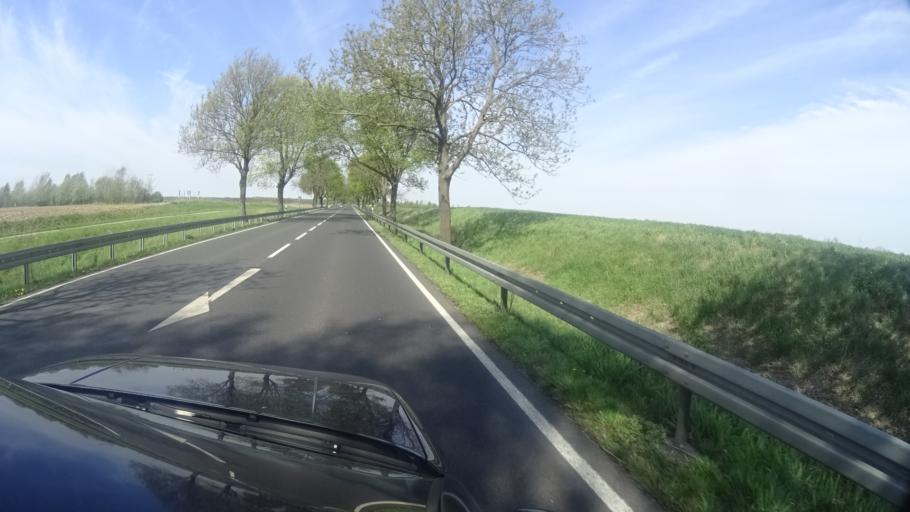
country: DE
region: Brandenburg
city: Paulinenaue
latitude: 52.6205
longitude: 12.7703
